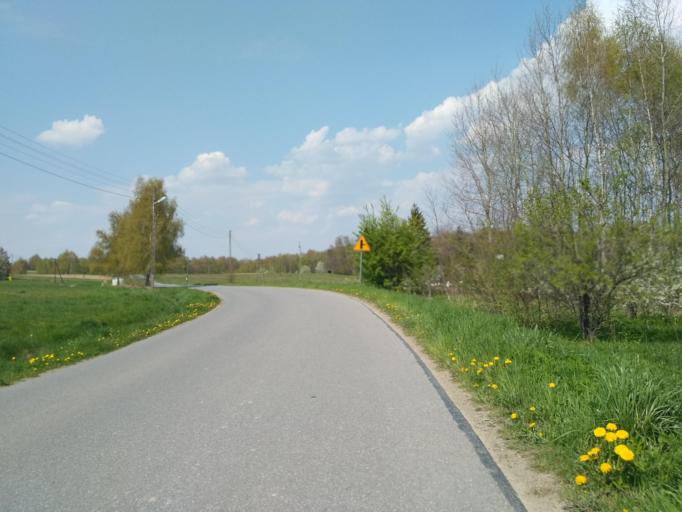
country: PL
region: Subcarpathian Voivodeship
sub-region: Powiat jasielski
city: Osiek Jasielski
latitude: 49.6811
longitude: 21.5099
